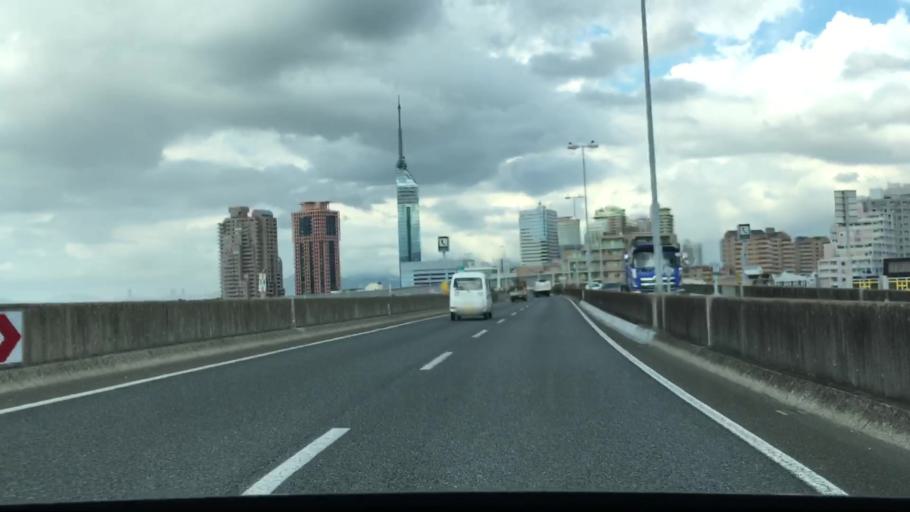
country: JP
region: Fukuoka
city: Fukuoka-shi
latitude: 33.5882
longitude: 130.3425
